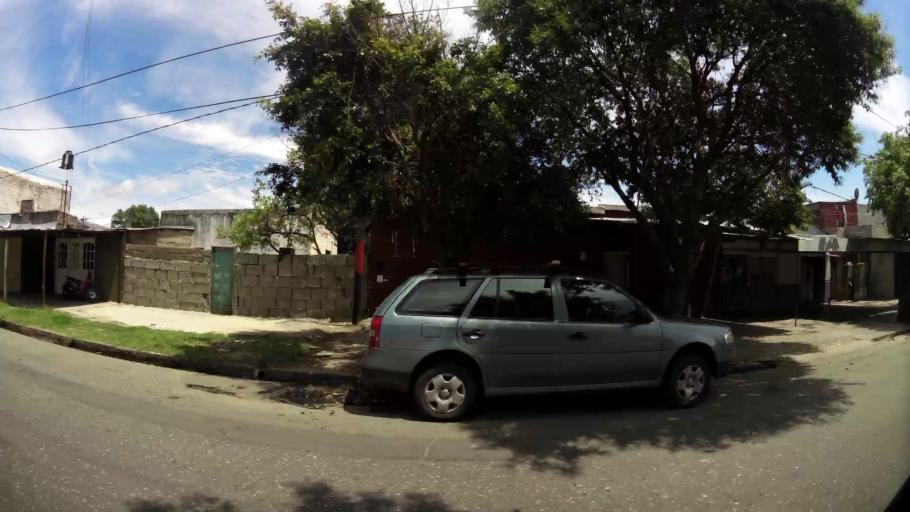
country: AR
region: Santa Fe
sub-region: Departamento de Rosario
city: Rosario
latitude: -32.9862
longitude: -60.6363
